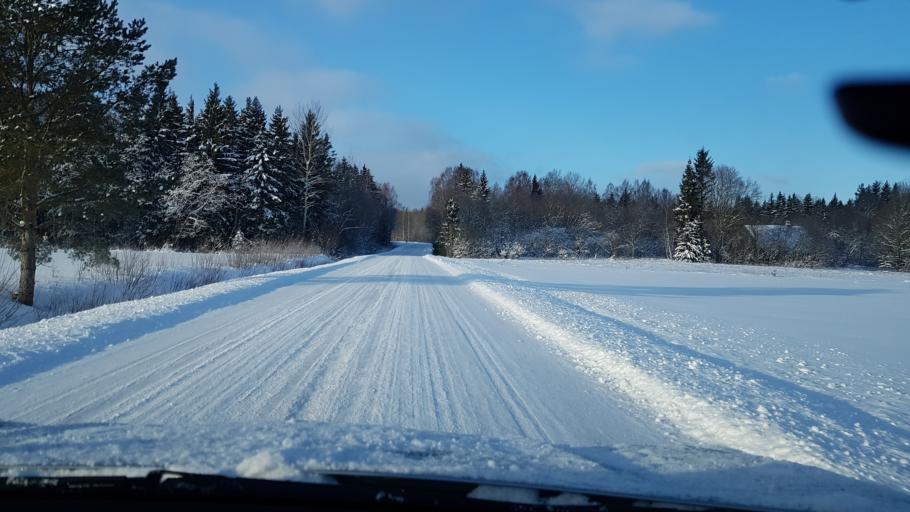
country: EE
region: Harju
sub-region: Nissi vald
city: Turba
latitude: 59.1032
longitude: 24.2448
